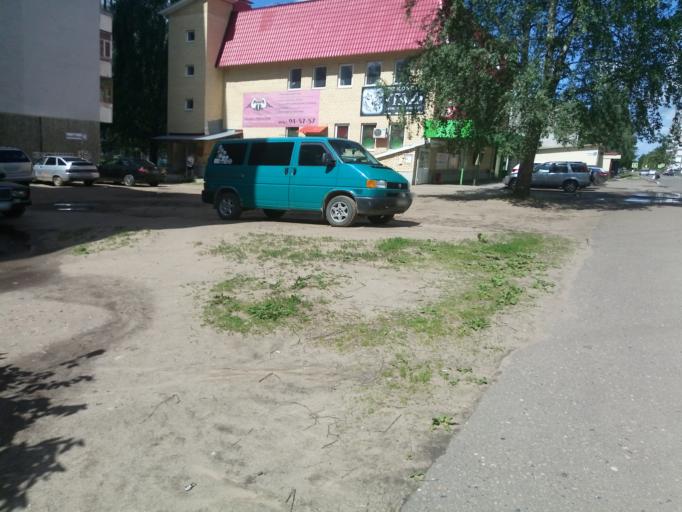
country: RU
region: Jaroslavl
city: Yaroslavl
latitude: 57.6542
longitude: 39.9605
